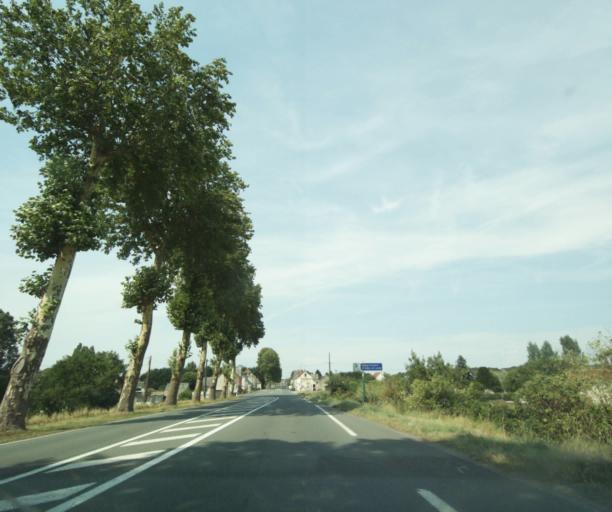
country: FR
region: Centre
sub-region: Departement d'Indre-et-Loire
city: La Celle-Saint-Avant
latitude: 47.0071
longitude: 0.6006
